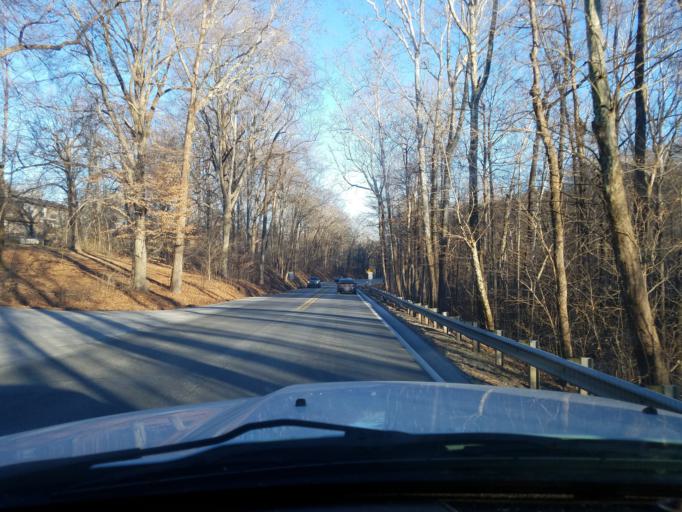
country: US
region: Indiana
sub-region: Floyd County
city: Galena
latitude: 38.3675
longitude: -85.9676
